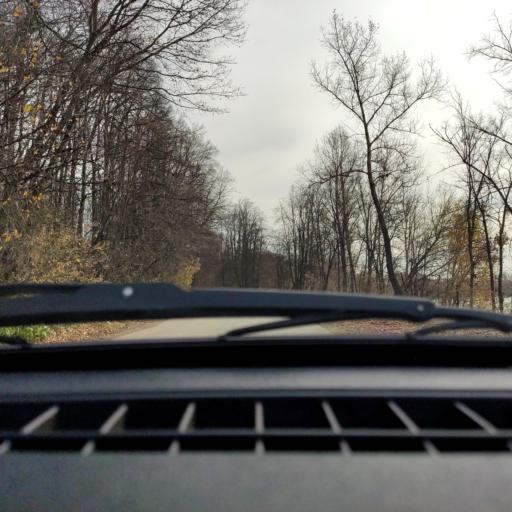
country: RU
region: Bashkortostan
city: Ufa
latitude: 54.7836
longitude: 56.1707
